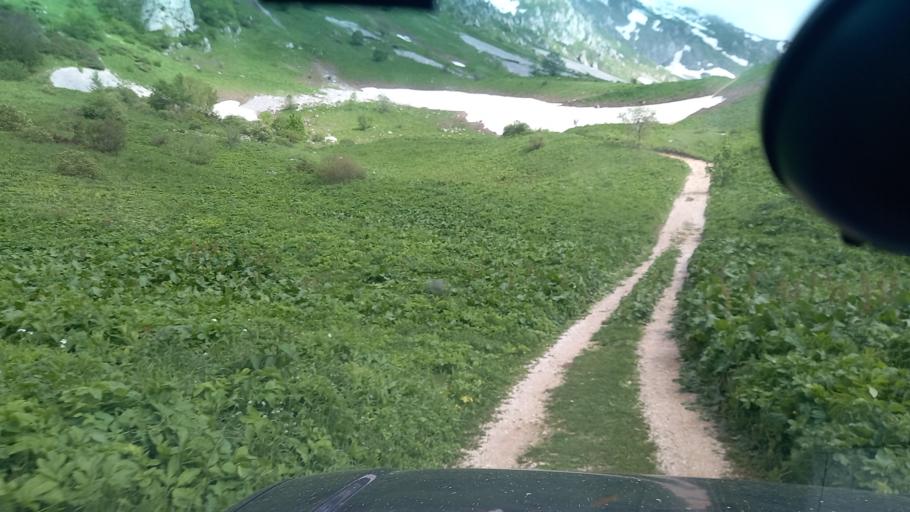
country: RU
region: Krasnodarskiy
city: Neftegorsk
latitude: 44.0114
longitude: 39.8599
